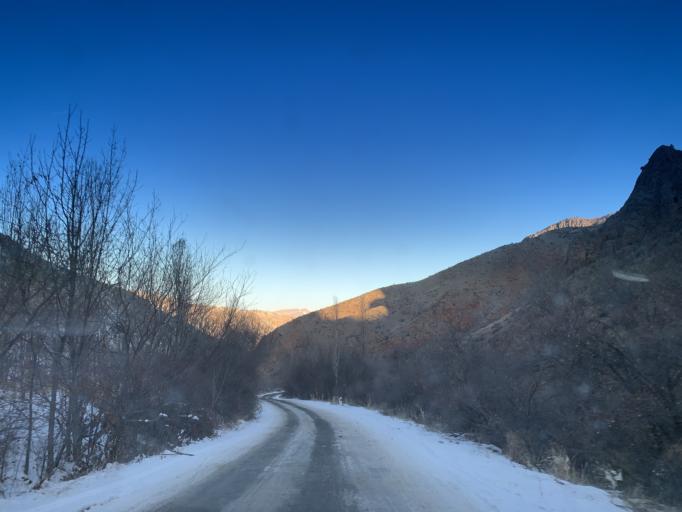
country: AM
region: Vayots' Dzori Marz
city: Areni
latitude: 39.6833
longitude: 45.2300
